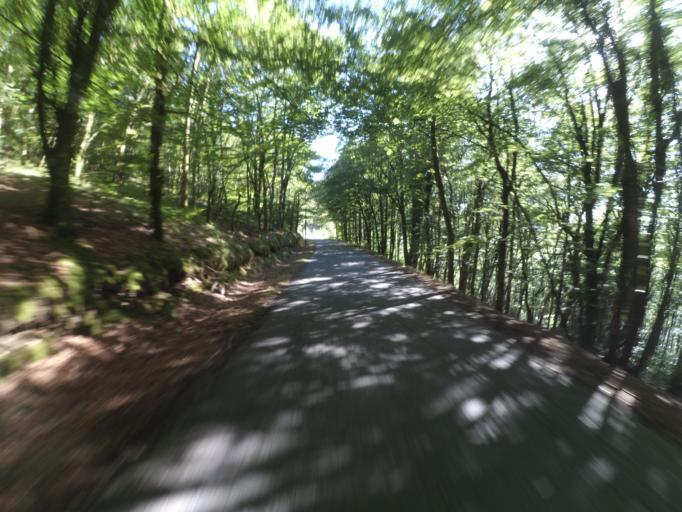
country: FR
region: Limousin
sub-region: Departement de la Correze
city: Bugeat
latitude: 45.6916
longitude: 1.9732
